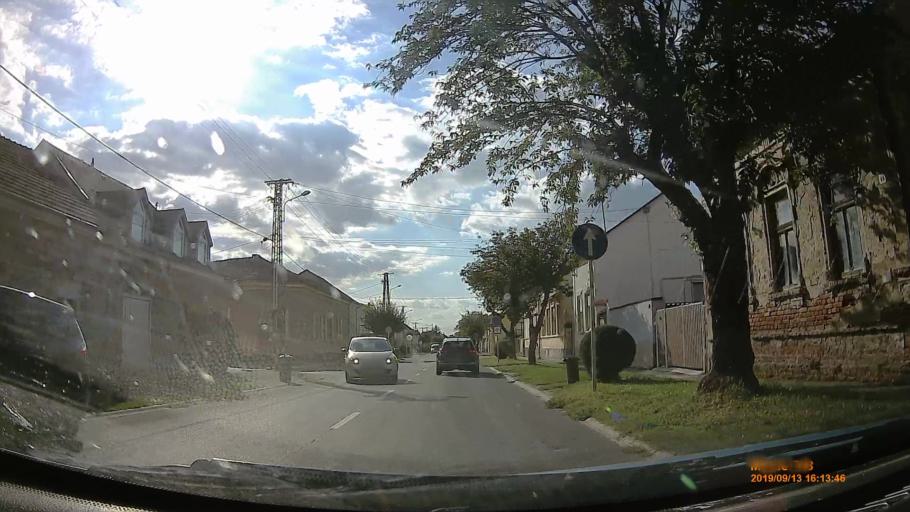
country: HU
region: Zala
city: Nagykanizsa
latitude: 46.4636
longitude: 16.9896
